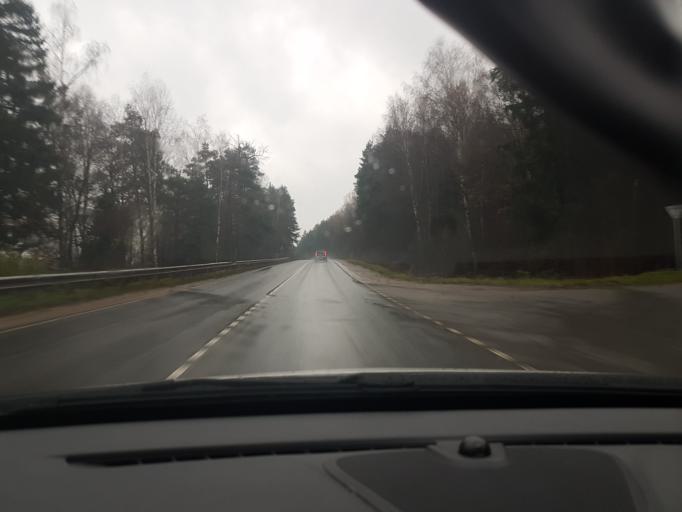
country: RU
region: Moskovskaya
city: Snegiri
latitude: 55.8539
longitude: 36.9388
